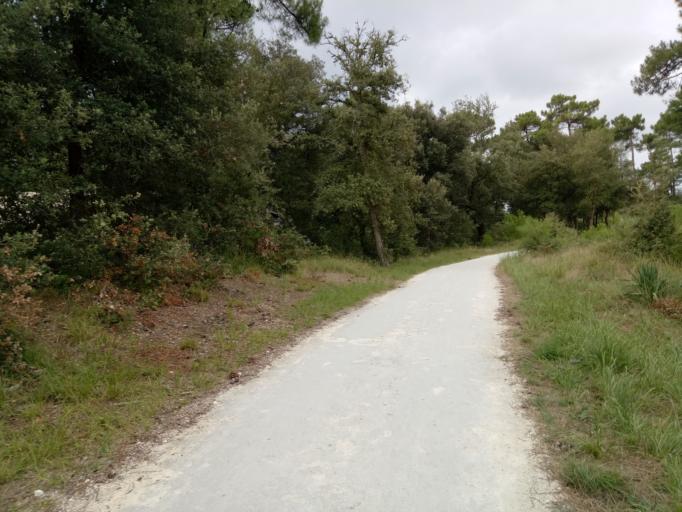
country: FR
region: Poitou-Charentes
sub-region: Departement de la Charente-Maritime
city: Saint-Trojan-les-Bains
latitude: 45.8636
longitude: -1.2435
